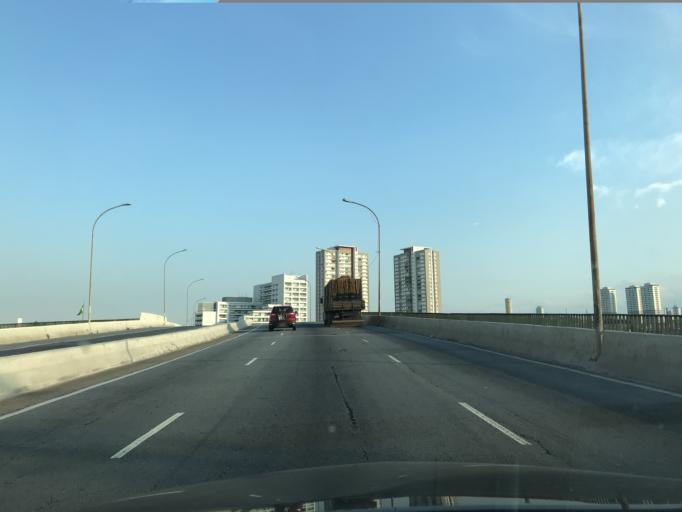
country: BR
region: Sao Paulo
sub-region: Osasco
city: Osasco
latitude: -23.5254
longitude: -46.7411
